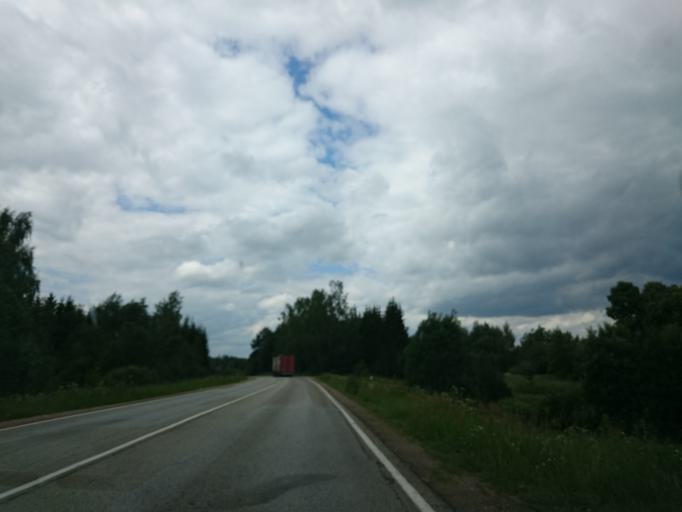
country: LV
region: Ludzas Rajons
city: Ludza
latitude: 56.5361
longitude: 27.5801
